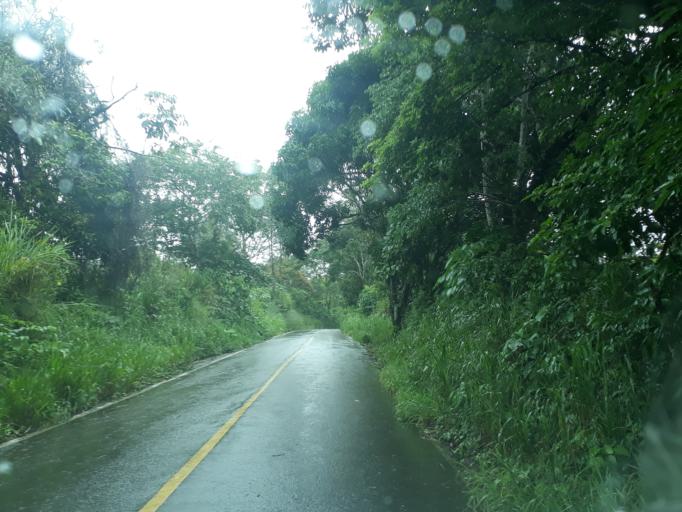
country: CO
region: Cundinamarca
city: Paratebueno
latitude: 4.4002
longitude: -73.3031
